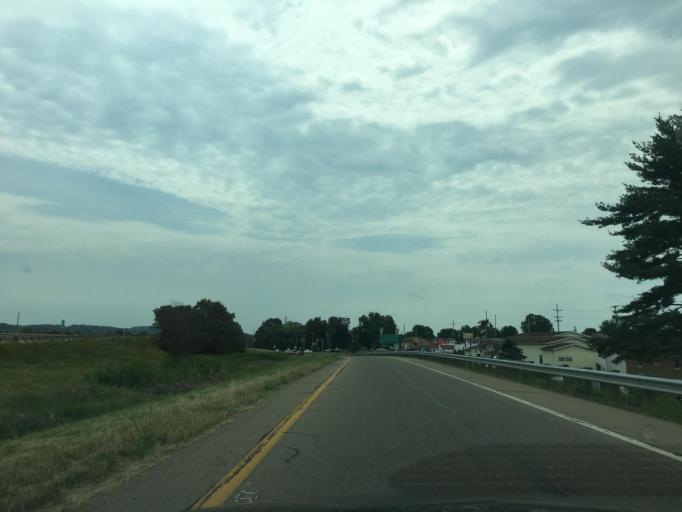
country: US
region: Ohio
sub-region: Tuscarawas County
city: New Philadelphia
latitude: 40.4801
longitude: -81.4518
